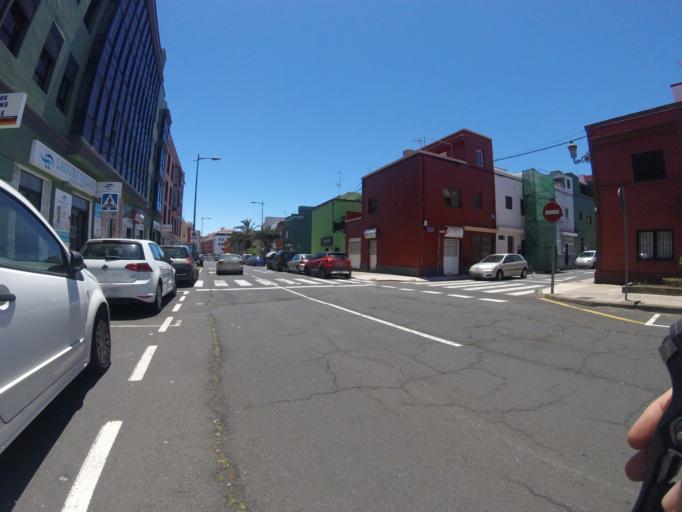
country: ES
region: Canary Islands
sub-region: Provincia de Santa Cruz de Tenerife
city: La Laguna
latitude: 28.4881
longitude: -16.3208
